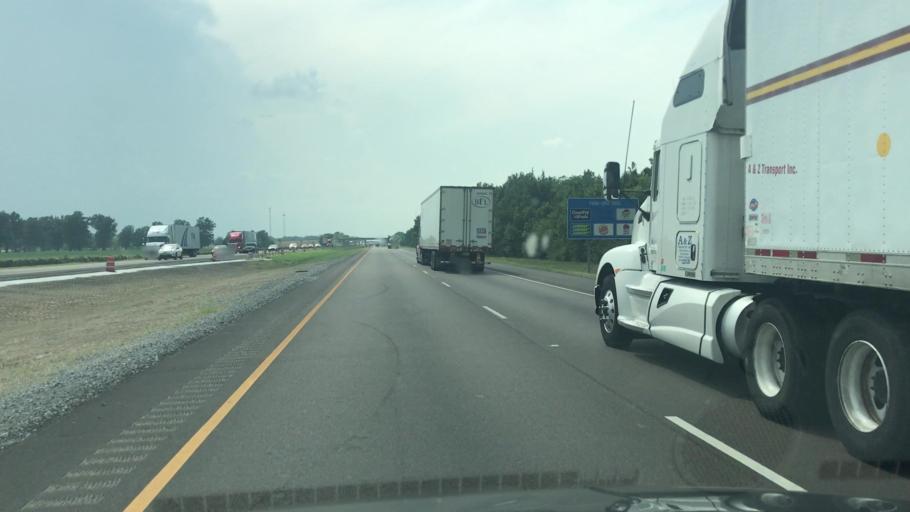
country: US
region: Arkansas
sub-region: Crittenden County
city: Earle
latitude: 35.1337
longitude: -90.4578
